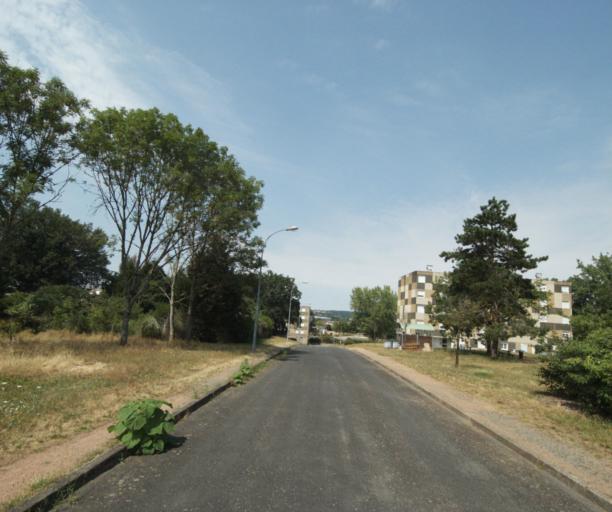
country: FR
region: Bourgogne
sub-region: Departement de Saone-et-Loire
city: Gueugnon
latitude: 46.5936
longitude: 4.0684
